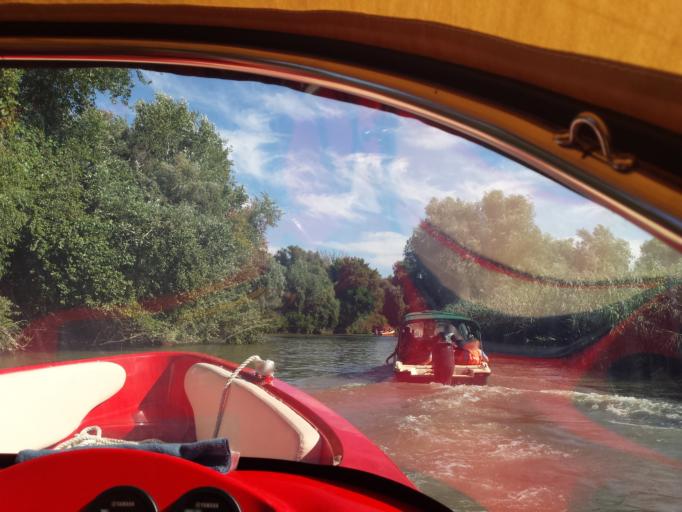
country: RO
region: Tulcea
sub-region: Comuna Pardina
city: Pardina
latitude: 45.2450
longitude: 29.0135
